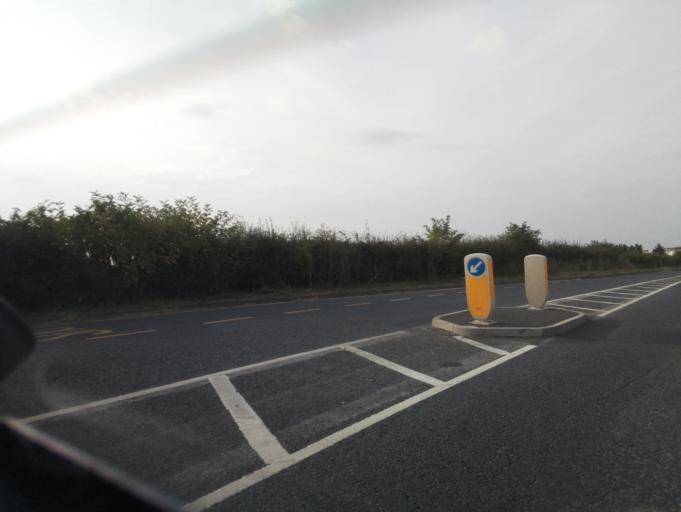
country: GB
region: England
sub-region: Gloucestershire
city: Gotherington
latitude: 51.9660
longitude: -2.0700
